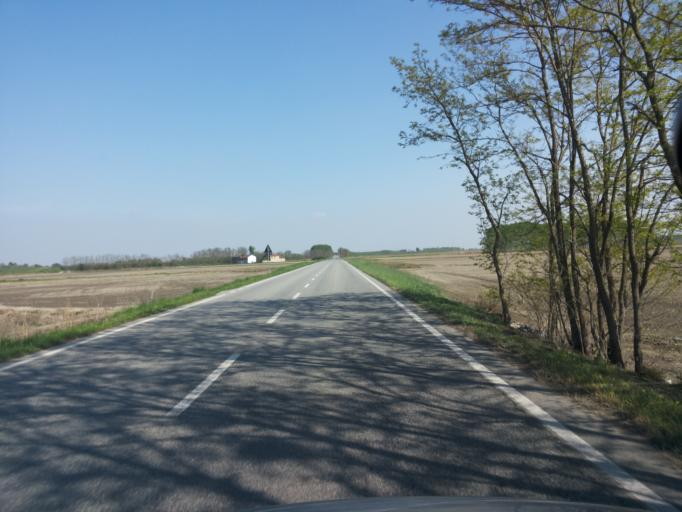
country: IT
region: Piedmont
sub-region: Provincia di Vercelli
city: Motta De Conti
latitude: 45.2097
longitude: 8.5246
